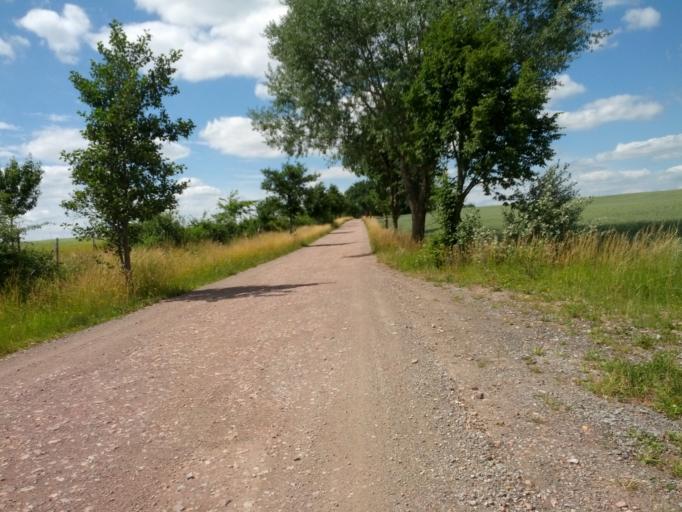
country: DE
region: Thuringia
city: Bischofroda
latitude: 51.0173
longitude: 10.3461
